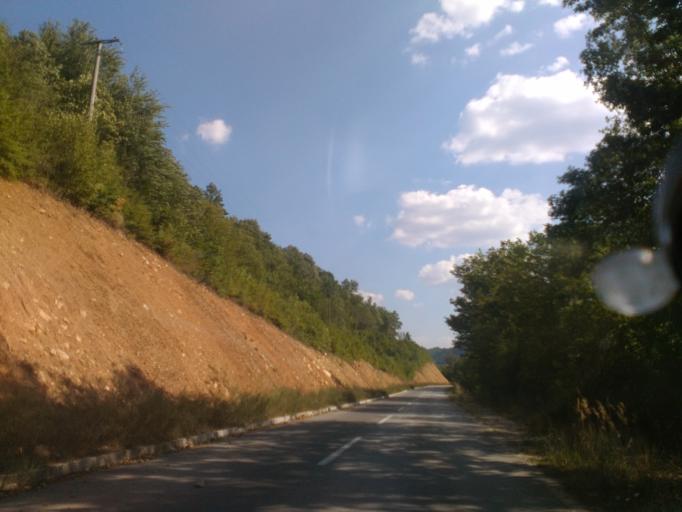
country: BA
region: Federation of Bosnia and Herzegovina
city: Orasac
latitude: 44.5055
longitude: 16.1294
